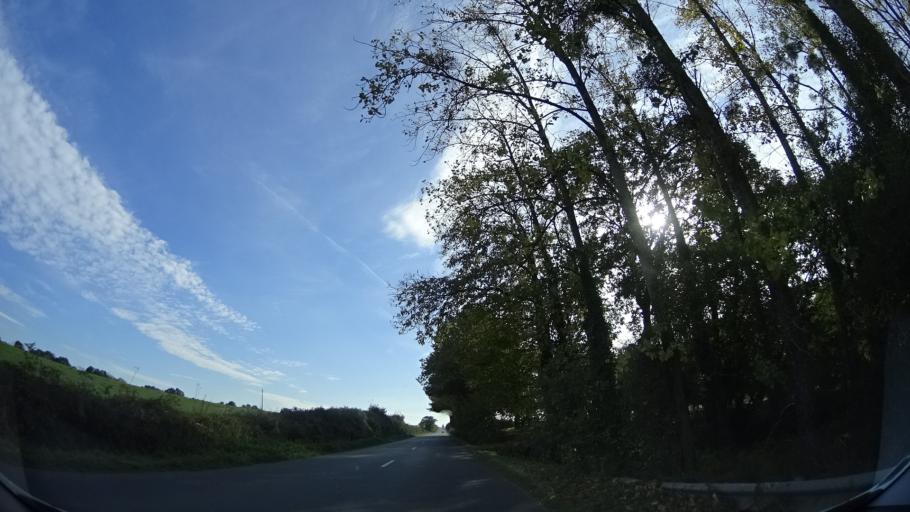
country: FR
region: Brittany
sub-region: Departement d'Ille-et-Vilaine
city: Bedee
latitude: 48.2059
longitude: -1.9410
